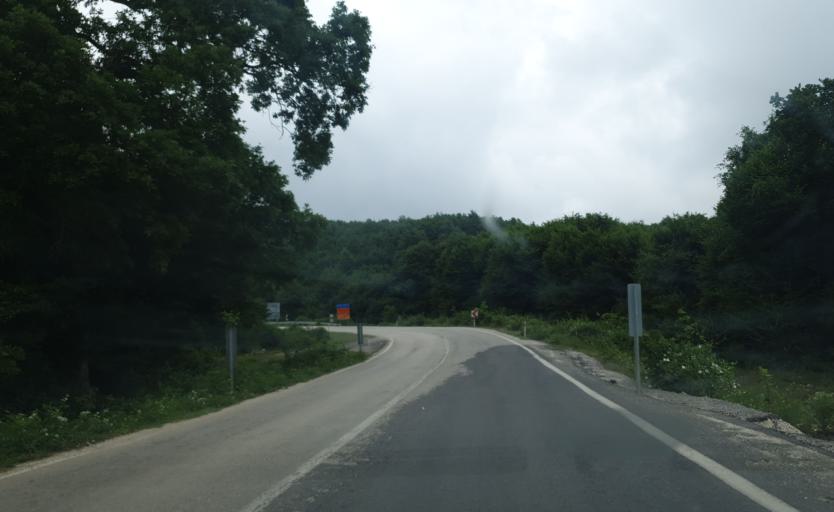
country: TR
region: Kirklareli
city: Salmydessus
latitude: 41.5854
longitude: 28.0704
